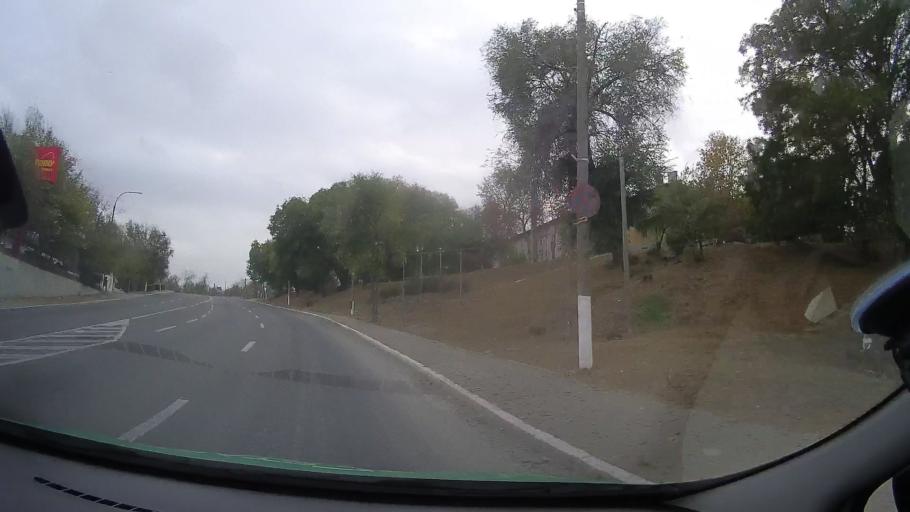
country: RO
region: Constanta
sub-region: Municipiul Medgidia
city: Medgidia
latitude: 44.2457
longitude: 28.2597
